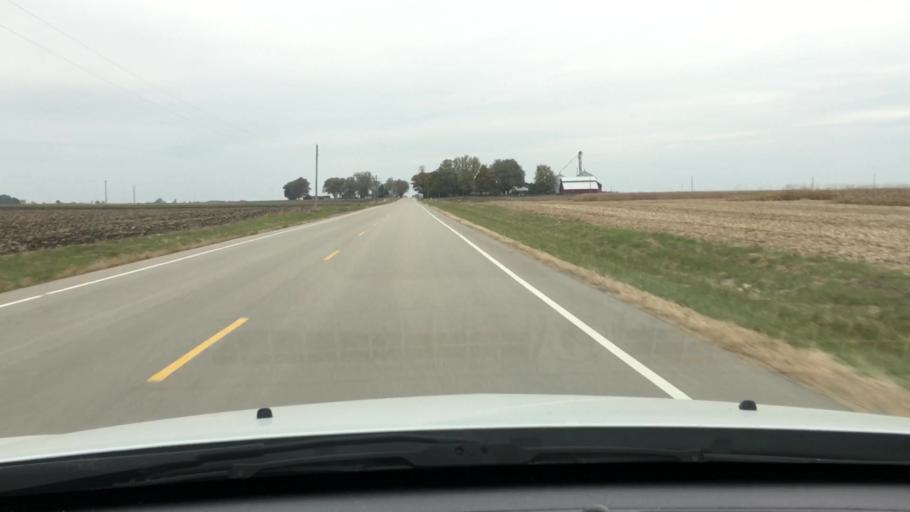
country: US
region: Illinois
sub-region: DeKalb County
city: Malta
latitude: 41.8166
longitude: -88.8864
